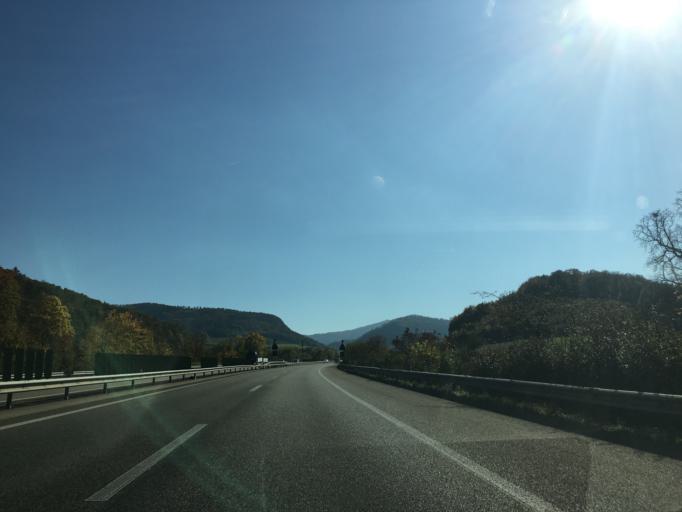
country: CH
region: Basel-Landschaft
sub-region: Bezirk Sissach
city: Tenniken
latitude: 47.4264
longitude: 7.8093
